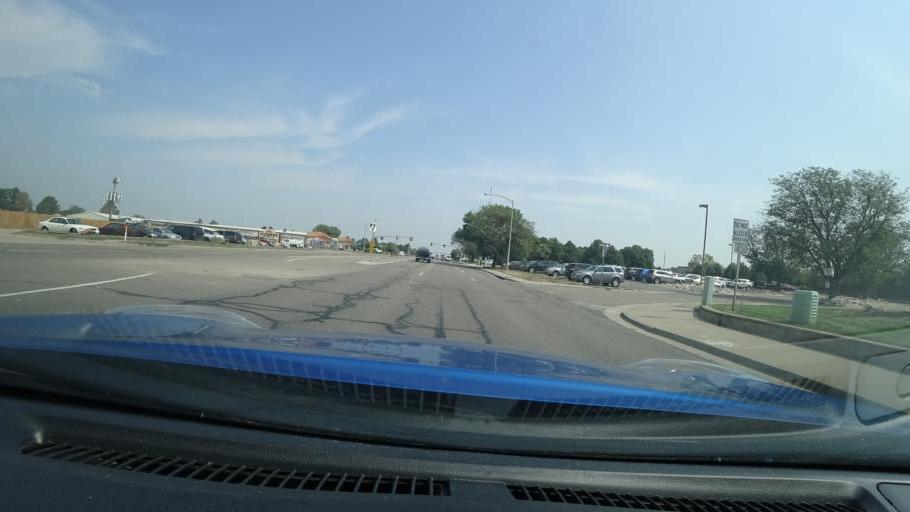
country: US
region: Colorado
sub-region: Adams County
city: Aurora
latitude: 39.7227
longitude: -104.7911
